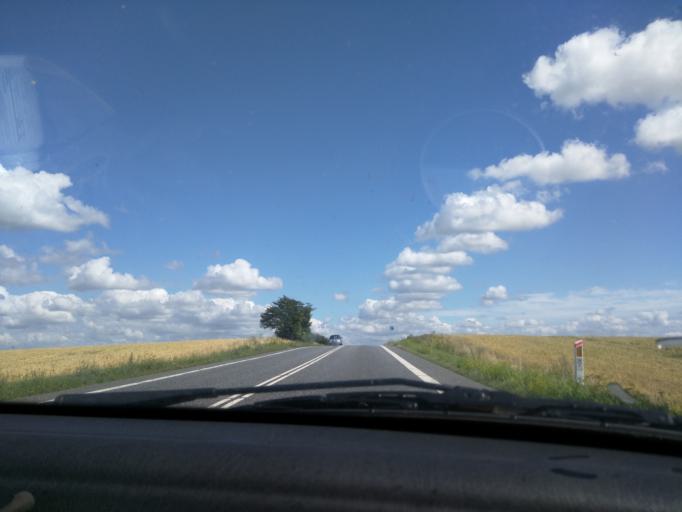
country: DK
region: Zealand
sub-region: Kalundborg Kommune
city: Kalundborg
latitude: 55.6747
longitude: 11.1863
